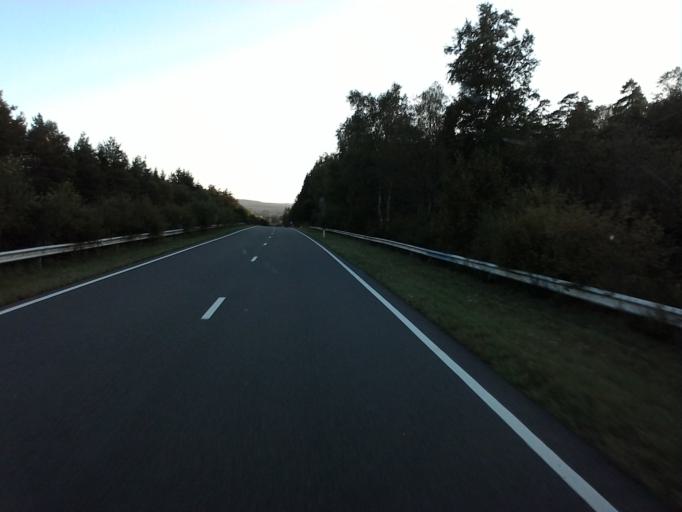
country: BE
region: Wallonia
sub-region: Province du Luxembourg
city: Saint-Hubert
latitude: 50.0481
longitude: 5.3952
